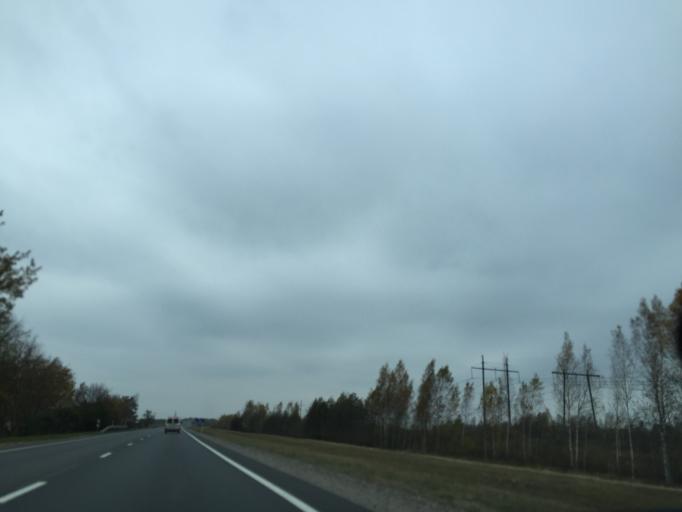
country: LV
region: Ozolnieku
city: Ozolnieki
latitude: 56.6614
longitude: 23.8148
